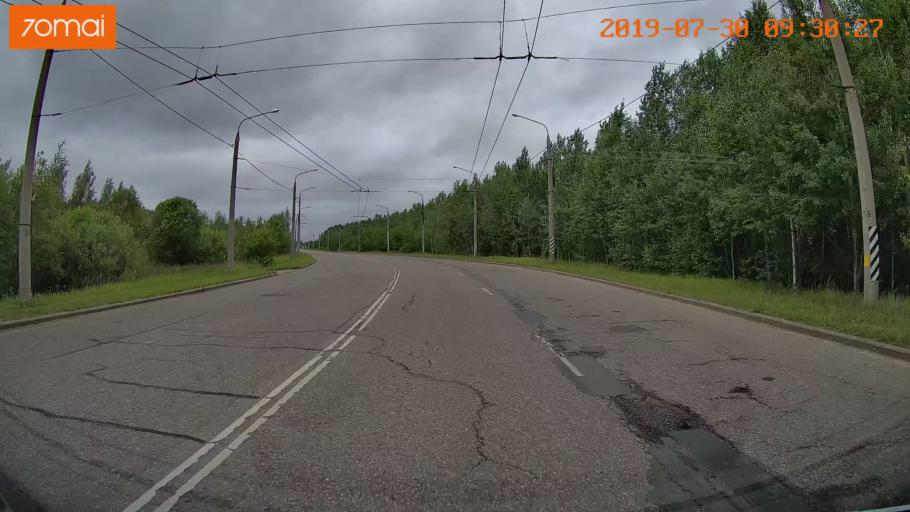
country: RU
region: Ivanovo
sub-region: Gorod Ivanovo
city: Ivanovo
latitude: 56.9446
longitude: 40.9465
